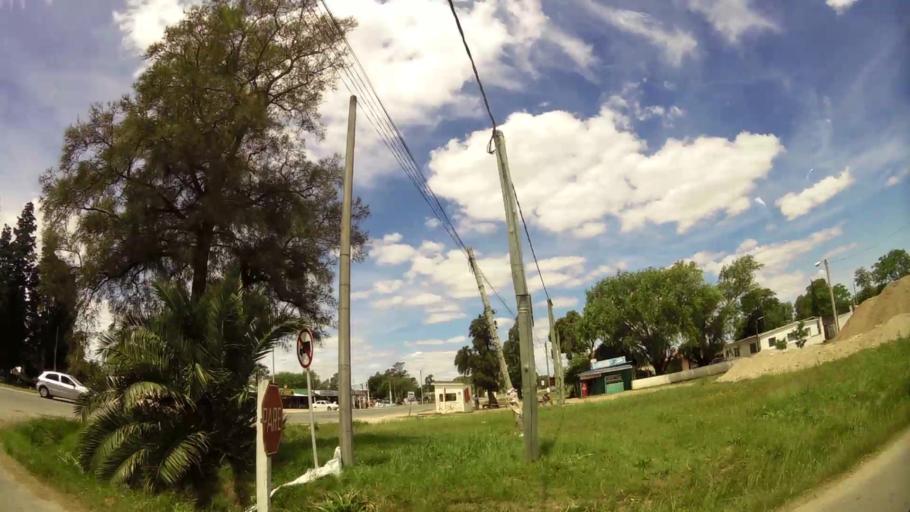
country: UY
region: San Jose
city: Delta del Tigre
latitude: -34.7497
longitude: -56.4197
